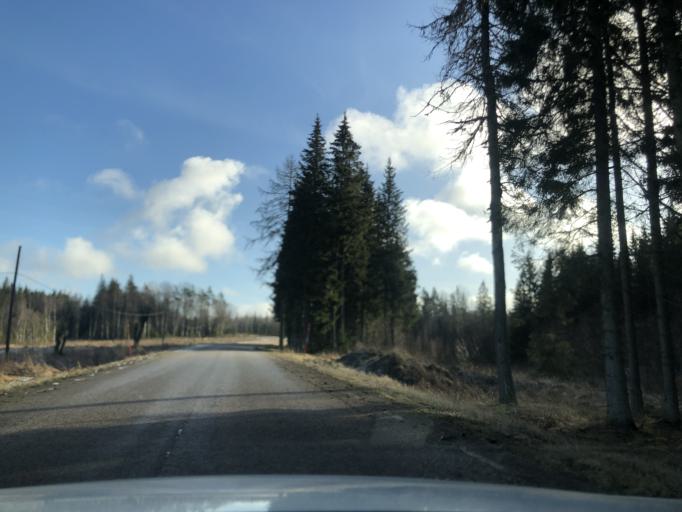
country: SE
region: Vaestra Goetaland
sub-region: Ulricehamns Kommun
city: Ulricehamn
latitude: 57.8036
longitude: 13.5598
